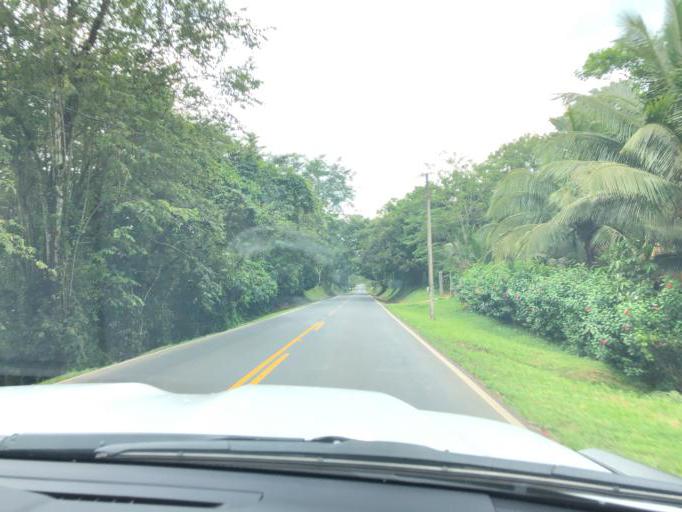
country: NI
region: Chontales
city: Villa Sandino
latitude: 11.9941
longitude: -84.7989
